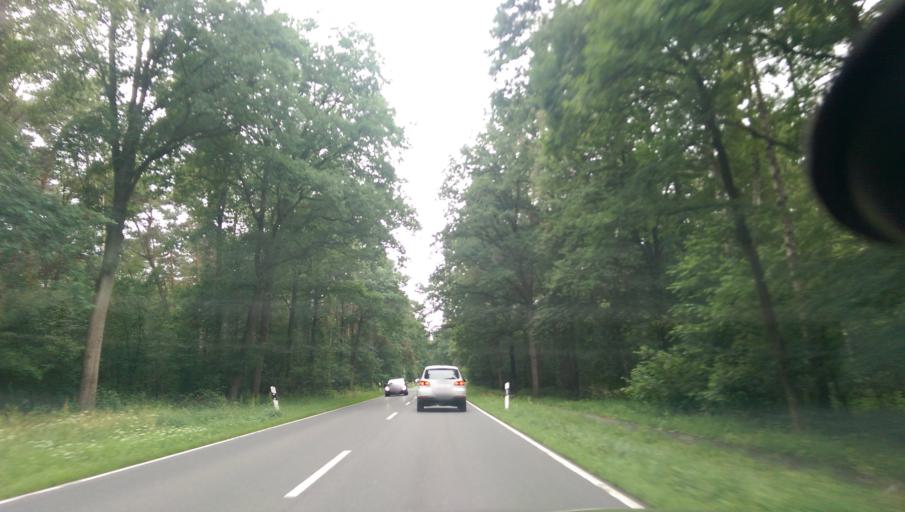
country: DE
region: Lower Saxony
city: Rotenburg
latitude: 53.0763
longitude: 9.4325
